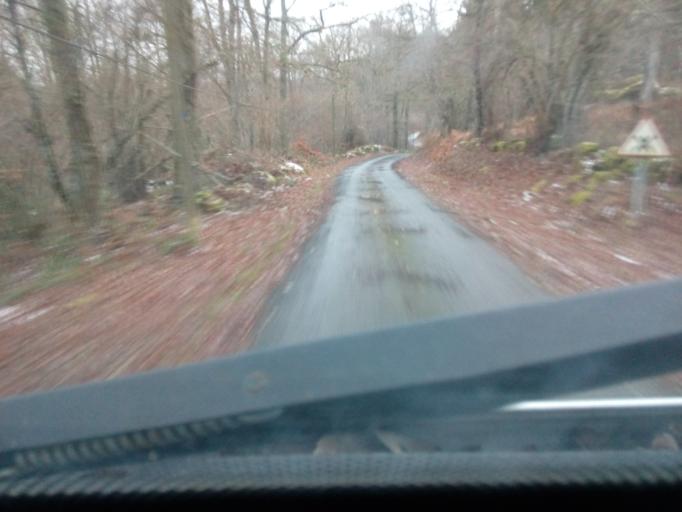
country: FR
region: Limousin
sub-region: Departement de la Creuse
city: Felletin
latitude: 45.8279
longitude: 2.2501
